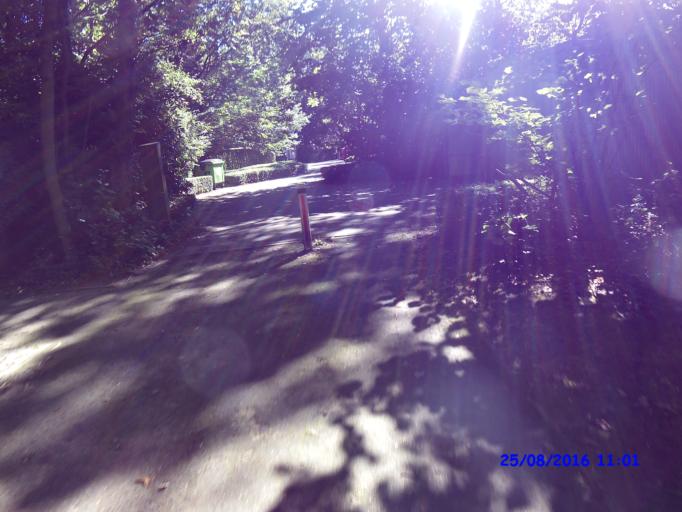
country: BE
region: Flanders
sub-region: Provincie Antwerpen
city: Beerse
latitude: 51.3145
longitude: 4.8542
